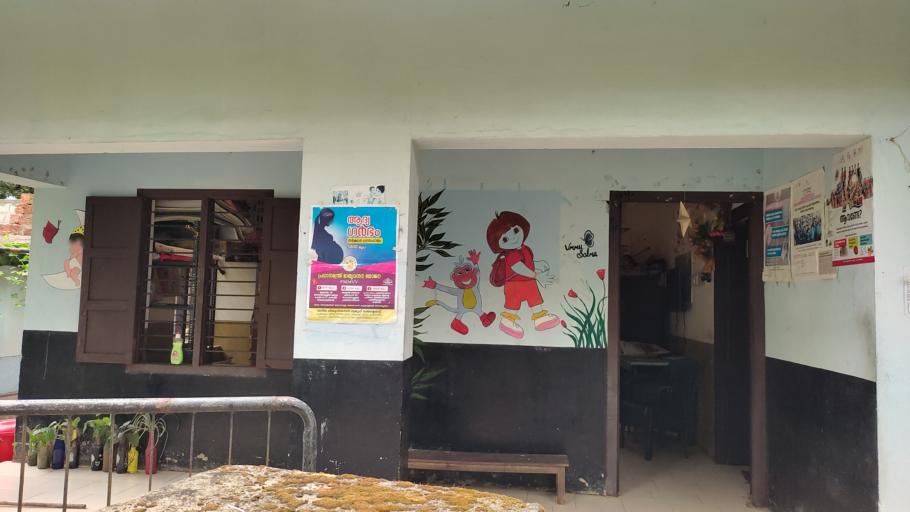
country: IN
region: Kerala
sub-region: Malappuram
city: Ponnani
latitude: 10.8393
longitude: 75.9661
